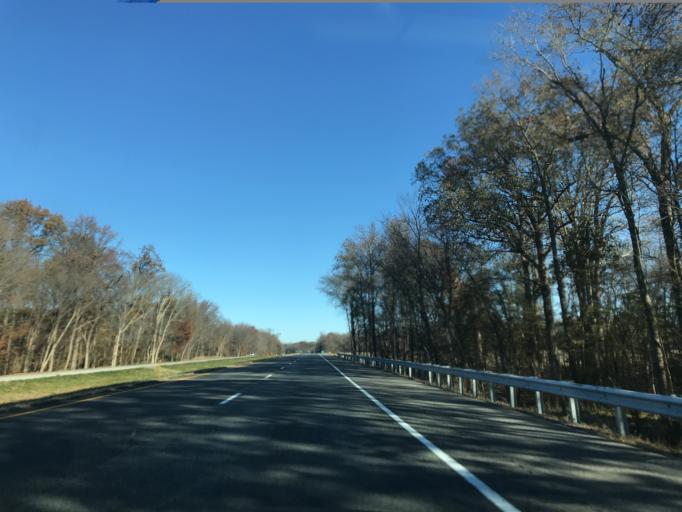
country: US
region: Maryland
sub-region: Queen Anne's County
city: Kingstown
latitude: 39.1332
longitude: -75.9328
